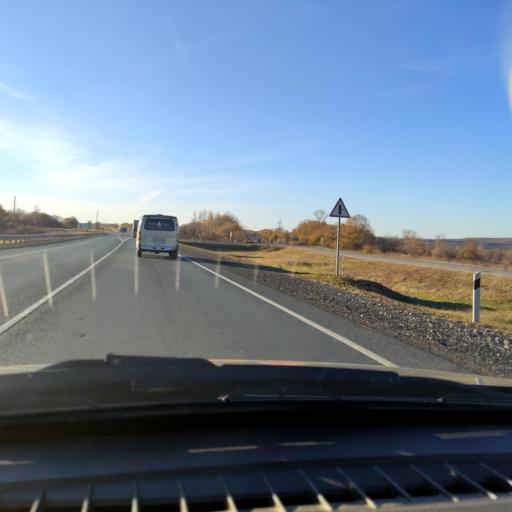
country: RU
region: Samara
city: Varlamovo
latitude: 53.1944
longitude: 48.3272
